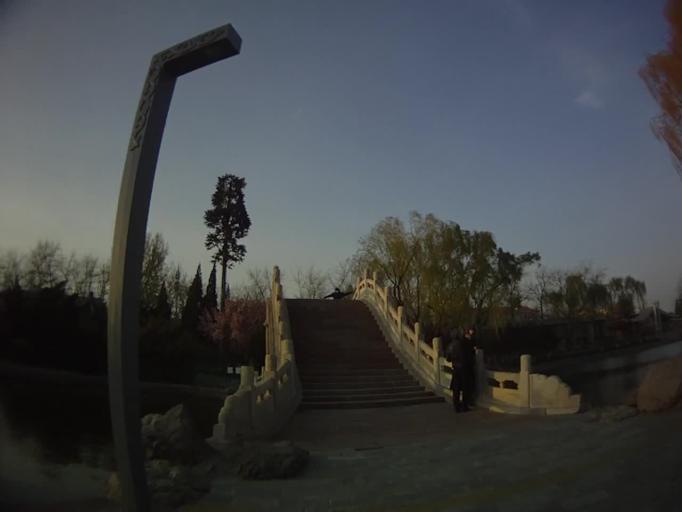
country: CN
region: Beijing
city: Longtan
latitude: 39.8791
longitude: 116.4331
